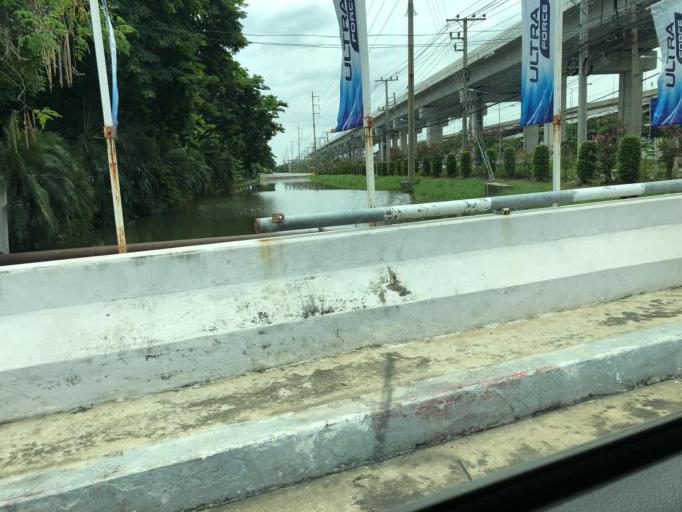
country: TH
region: Bangkok
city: Don Mueang
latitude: 13.9247
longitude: 100.6029
